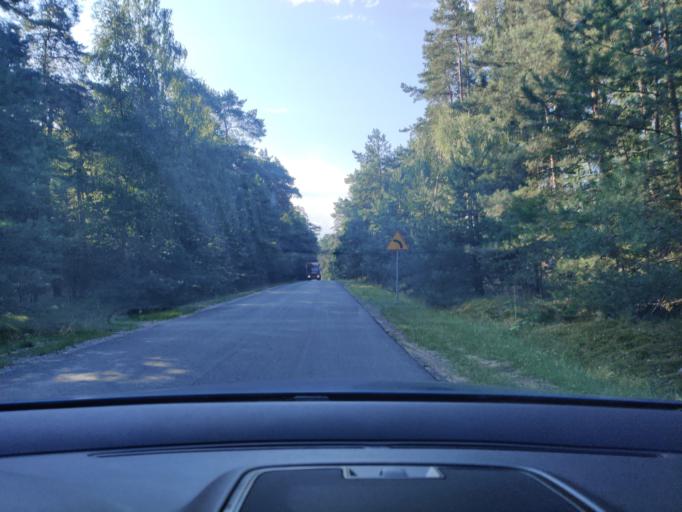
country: PL
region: Greater Poland Voivodeship
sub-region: Konin
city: Konin
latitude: 52.1789
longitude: 18.3353
